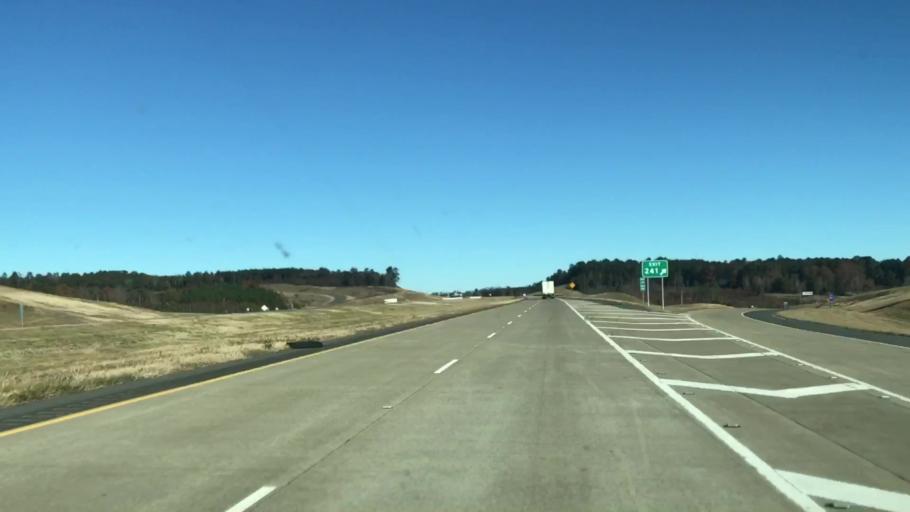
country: US
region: Louisiana
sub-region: Caddo Parish
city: Vivian
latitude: 32.9390
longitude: -93.8970
